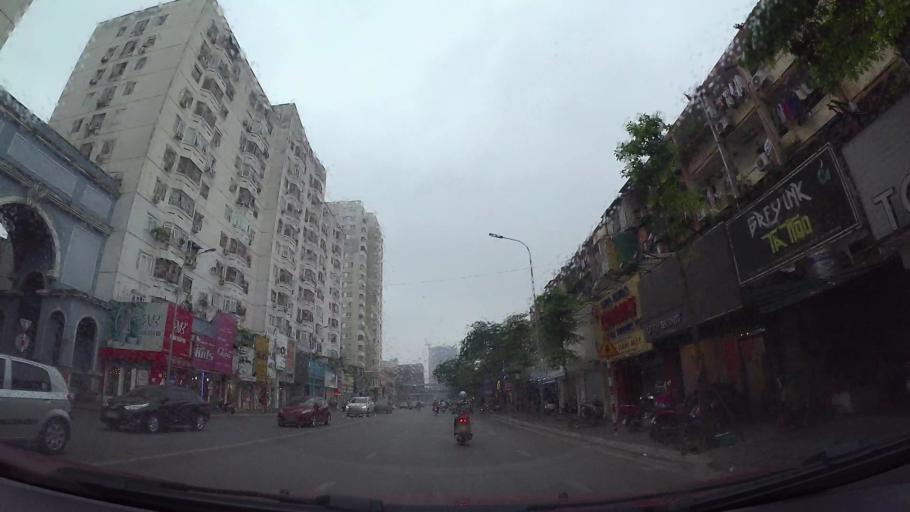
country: VN
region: Ha Noi
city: Dong Da
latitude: 21.0096
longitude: 105.8353
